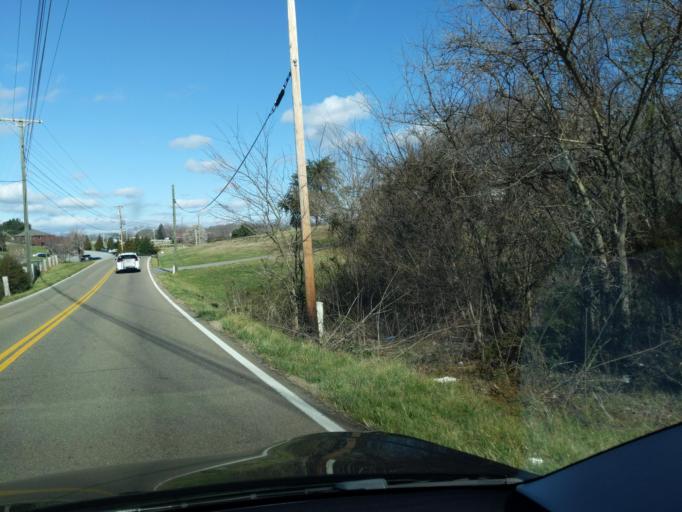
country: US
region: Tennessee
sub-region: Jefferson County
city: Dandridge
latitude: 35.9714
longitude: -83.5148
